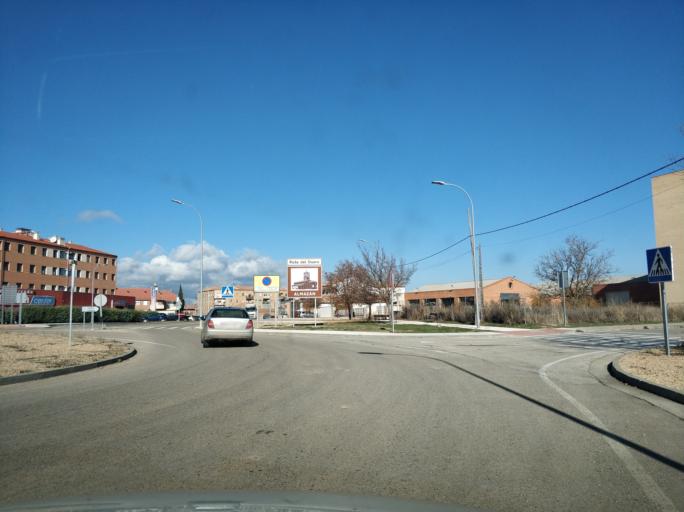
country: ES
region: Castille and Leon
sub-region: Provincia de Soria
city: Almazan
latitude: 41.4794
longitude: -2.5292
